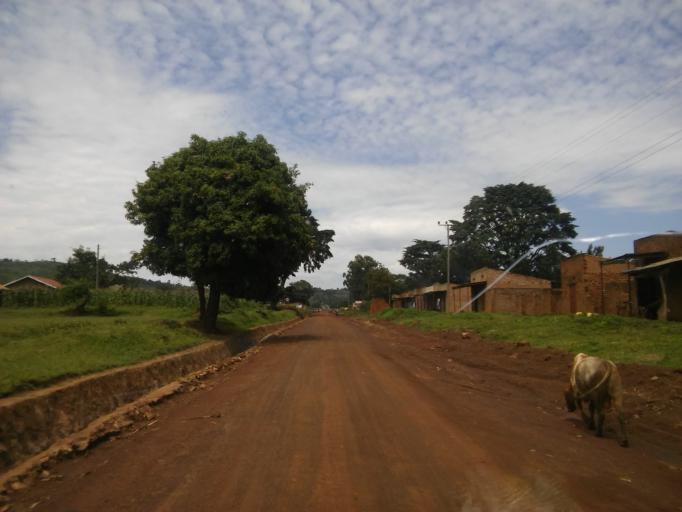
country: UG
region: Eastern Region
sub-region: Tororo District
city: Tororo
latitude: 0.8265
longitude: 34.2904
